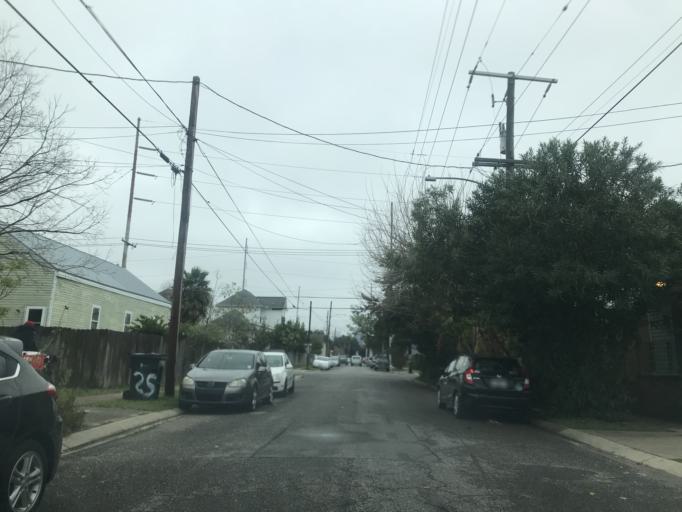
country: US
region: Louisiana
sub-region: Orleans Parish
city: New Orleans
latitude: 29.9693
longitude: -90.1012
